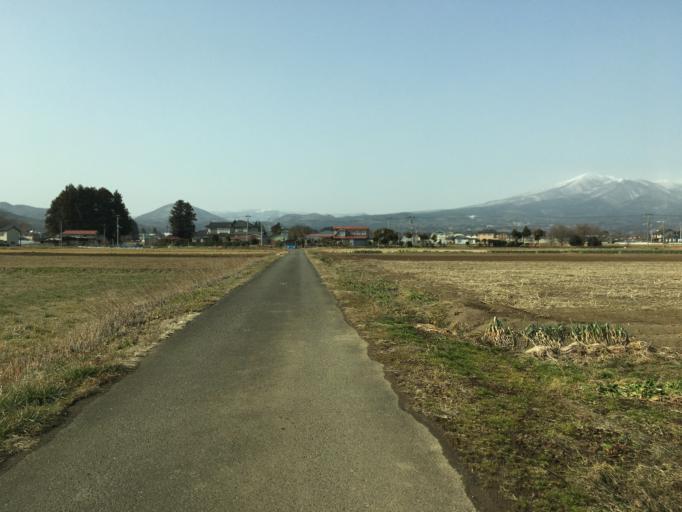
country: JP
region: Fukushima
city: Motomiya
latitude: 37.5362
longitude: 140.3807
